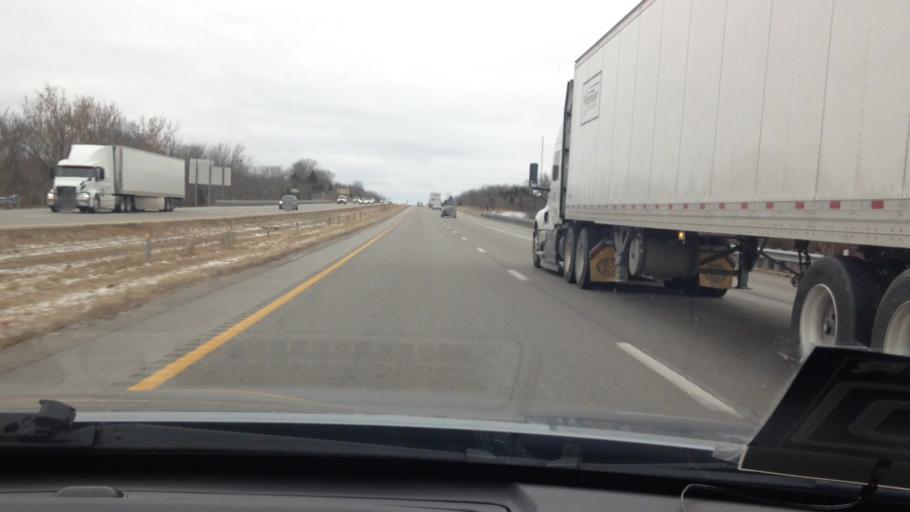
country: US
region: Missouri
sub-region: Platte County
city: Platte City
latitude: 39.4485
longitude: -94.7889
